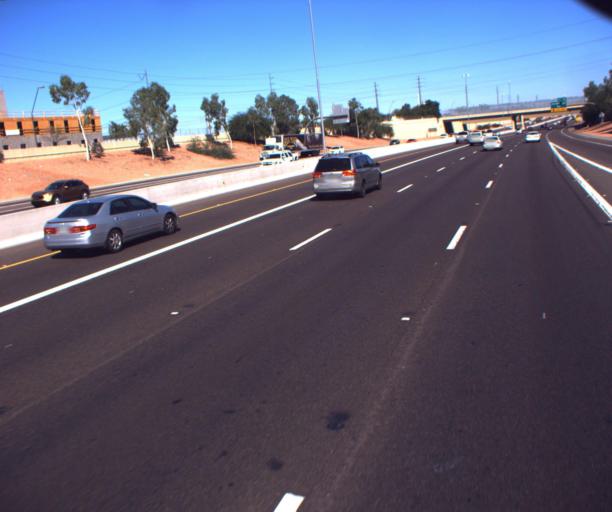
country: US
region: Arizona
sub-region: Maricopa County
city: San Carlos
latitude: 33.3538
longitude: -111.8942
